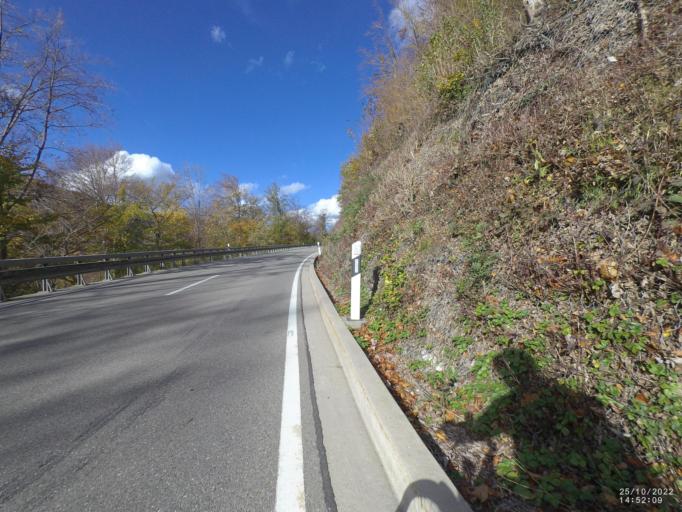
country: DE
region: Baden-Wuerttemberg
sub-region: Regierungsbezirk Stuttgart
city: Bohmenkirch
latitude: 48.6584
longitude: 9.8951
